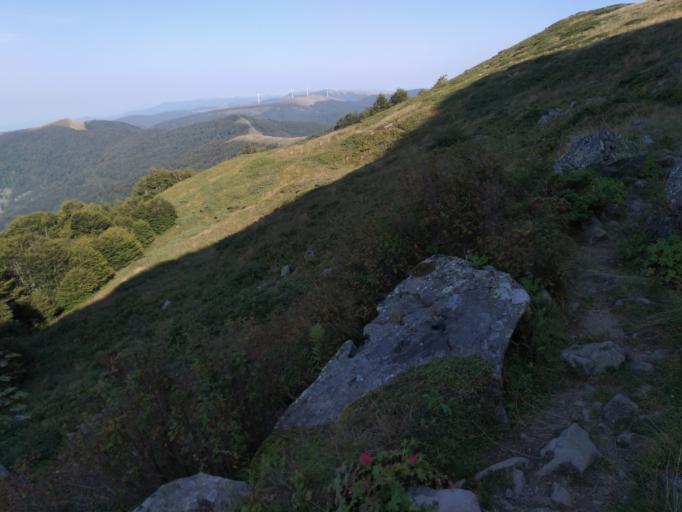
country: BG
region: Stara Zagora
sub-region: Obshtina Pavel Banya
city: Asen
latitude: 42.7622
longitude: 25.1080
